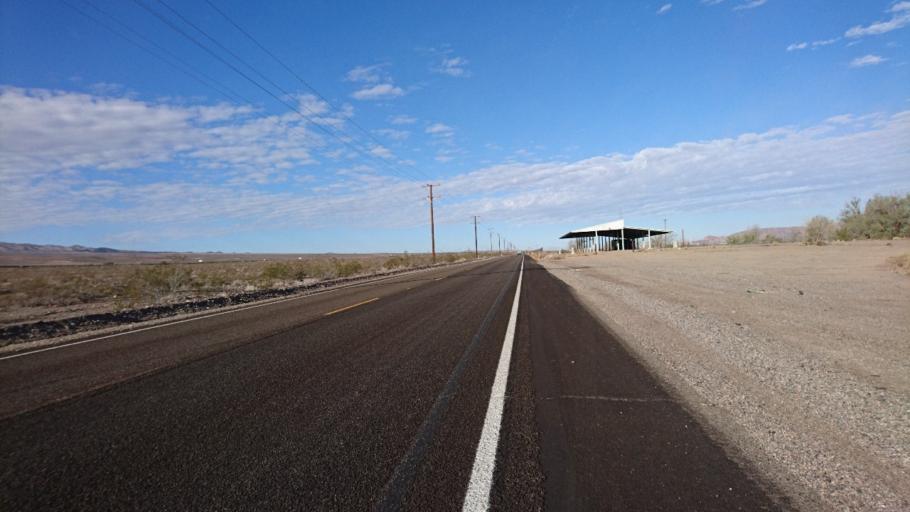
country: US
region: California
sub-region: San Bernardino County
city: Barstow
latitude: 34.8479
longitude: -116.7944
